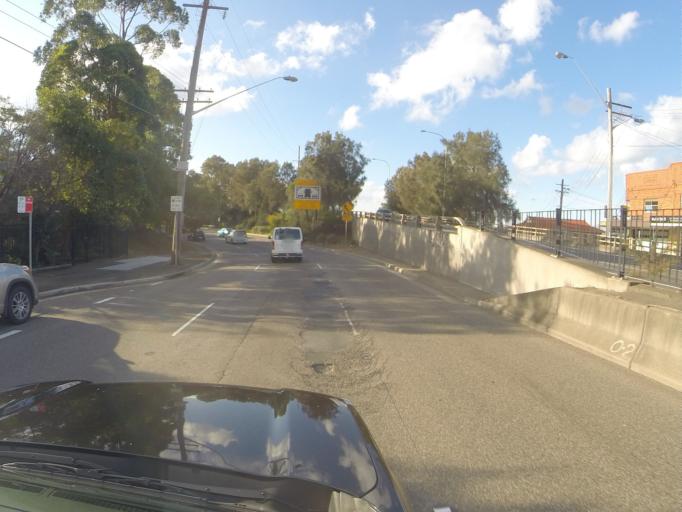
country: AU
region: New South Wales
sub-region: Kogarah
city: Blakehurst
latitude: -34.0066
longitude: 151.1120
